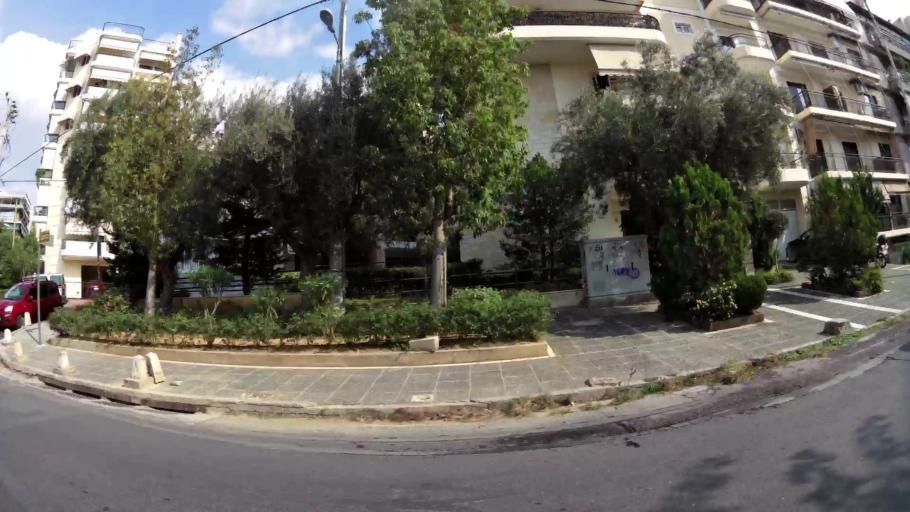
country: GR
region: Attica
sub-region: Nomarchia Athinas
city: Nea Smyrni
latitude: 37.9387
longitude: 23.7162
